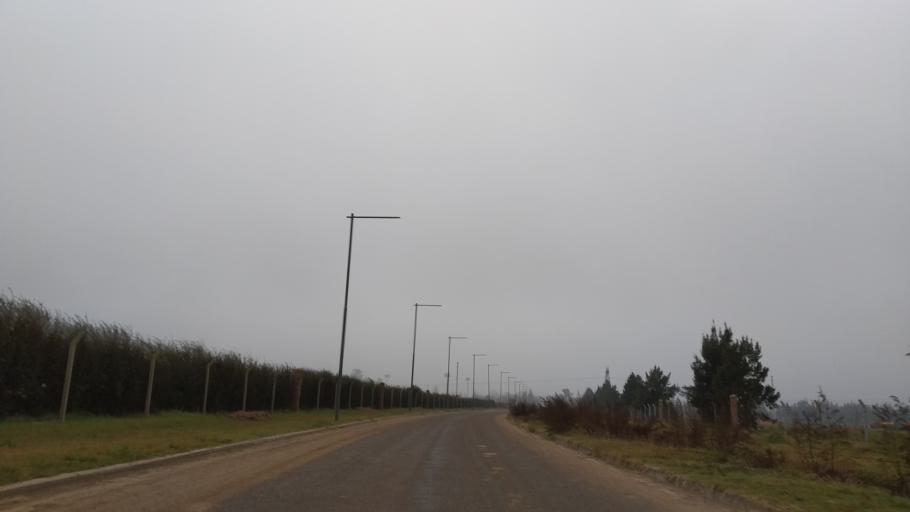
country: AR
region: Santa Fe
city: Funes
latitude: -32.9415
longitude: -60.7682
